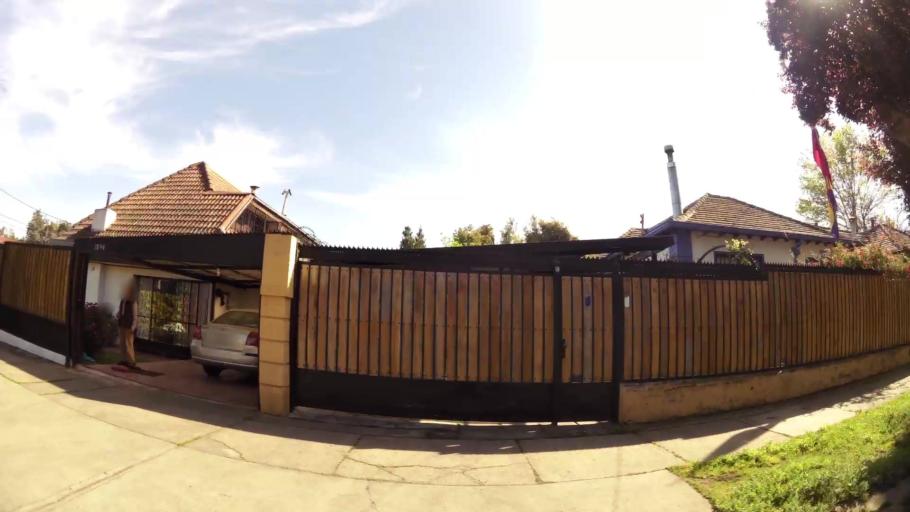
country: CL
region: Santiago Metropolitan
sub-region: Provincia de Santiago
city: Villa Presidente Frei, Nunoa, Santiago, Chile
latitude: -33.4526
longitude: -70.5538
